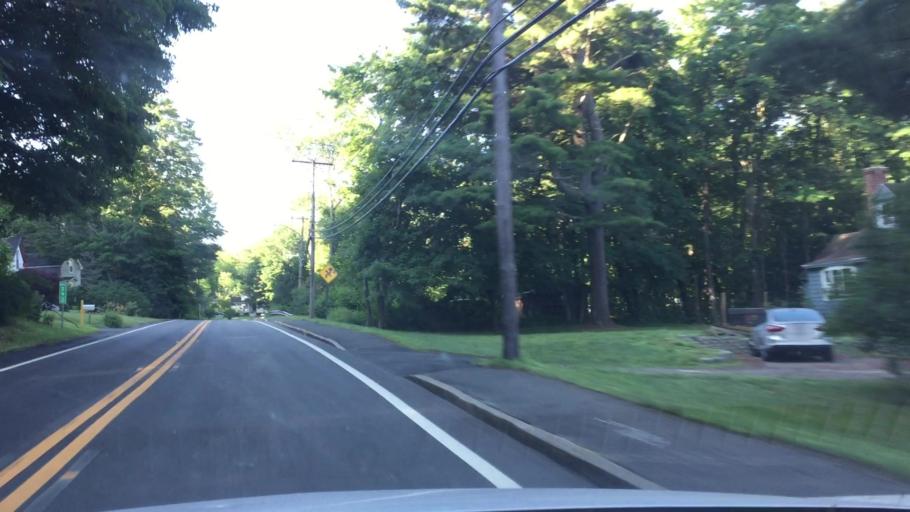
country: US
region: Massachusetts
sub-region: Berkshire County
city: Becket
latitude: 42.3270
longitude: -73.0835
